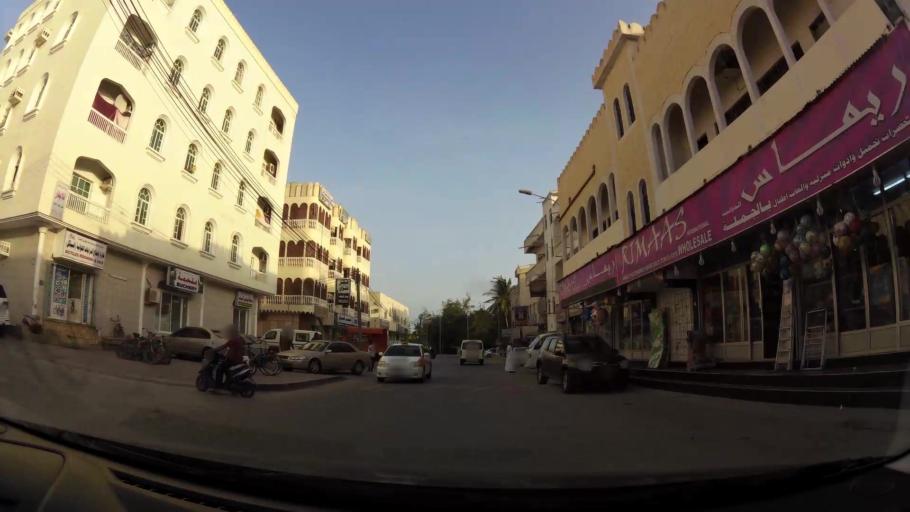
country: OM
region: Zufar
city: Salalah
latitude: 17.0134
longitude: 54.1032
